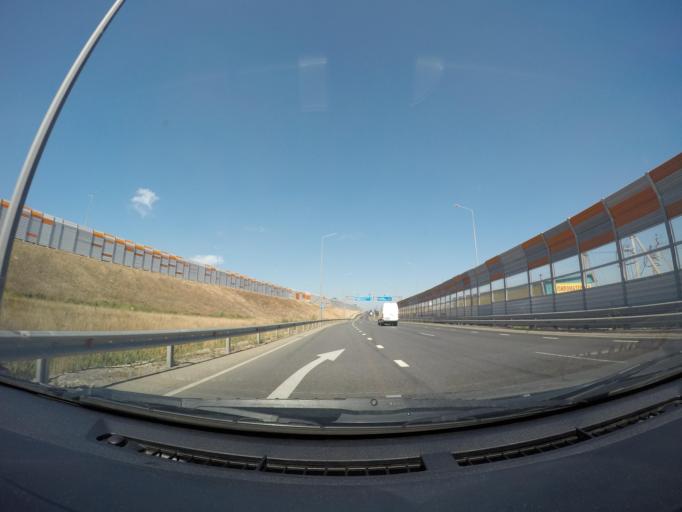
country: RU
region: Moskovskaya
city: Gzhel'
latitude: 55.6254
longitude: 38.3655
